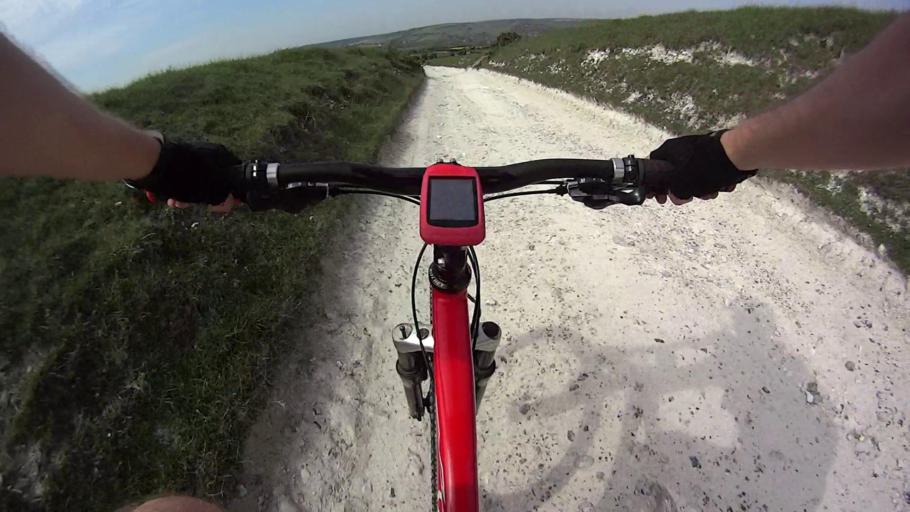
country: GB
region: England
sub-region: East Sussex
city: Seaford
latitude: 50.8090
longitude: 0.1769
